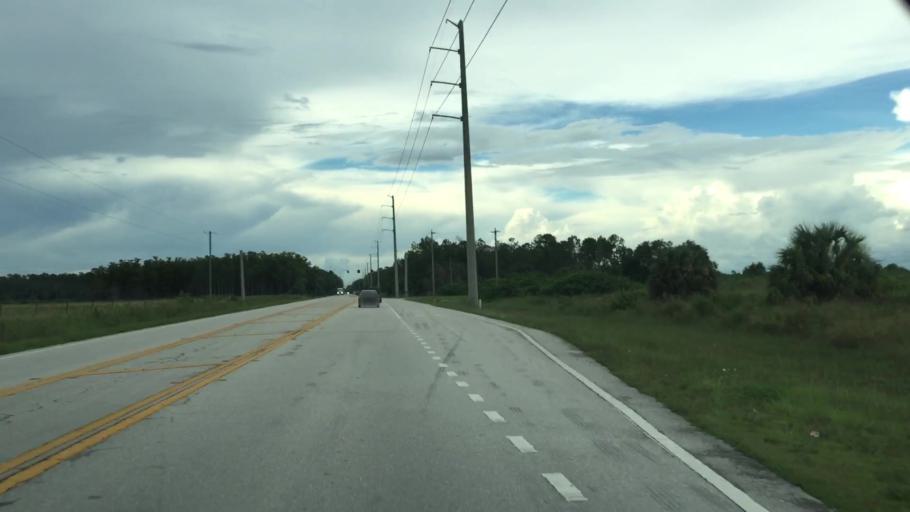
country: US
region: Florida
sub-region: Collier County
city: Orangetree
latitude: 26.3256
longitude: -81.5950
